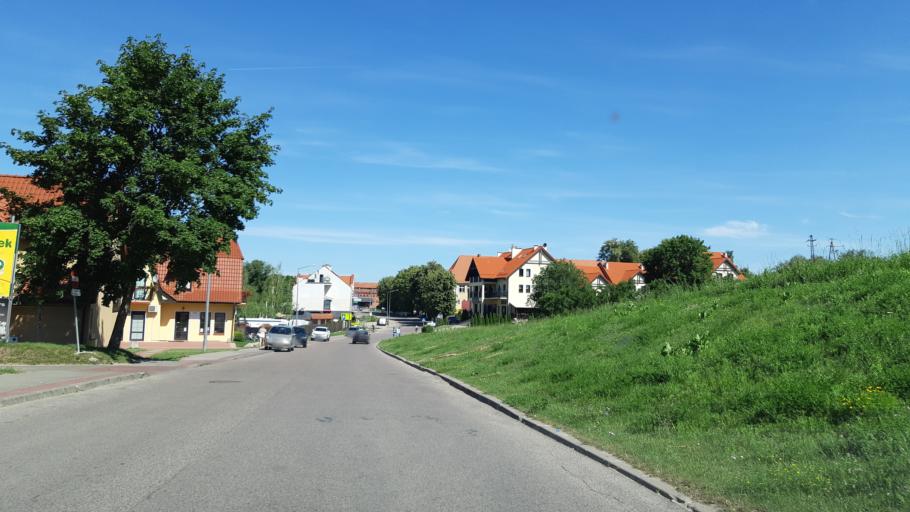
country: PL
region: Warmian-Masurian Voivodeship
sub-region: Powiat mragowski
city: Mikolajki
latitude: 53.8018
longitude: 21.5751
